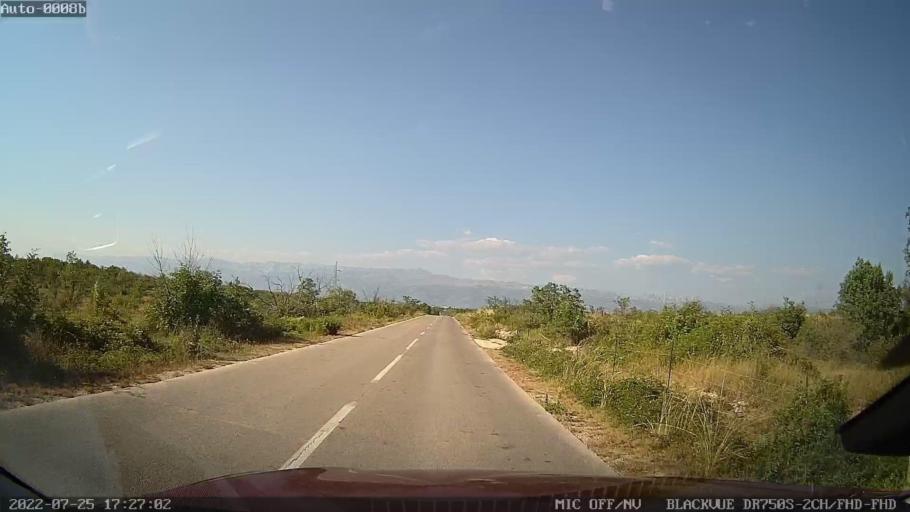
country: HR
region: Zadarska
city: Pridraga
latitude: 44.1392
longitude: 15.5031
